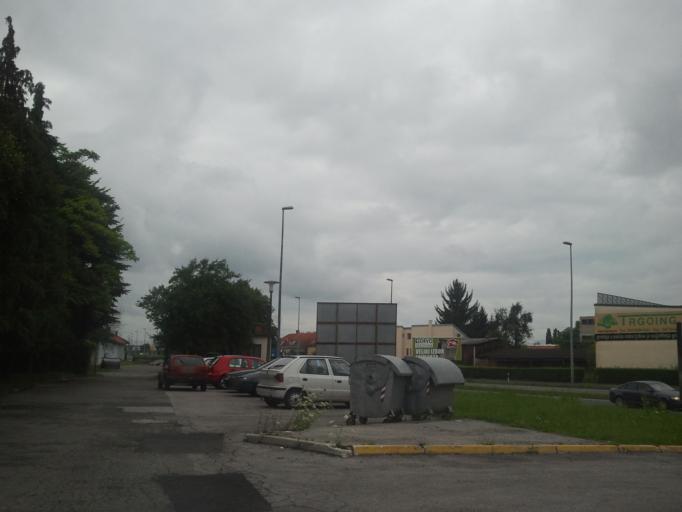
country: HR
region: Karlovacka
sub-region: Grad Karlovac
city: Karlovac
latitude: 45.5017
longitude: 15.5450
